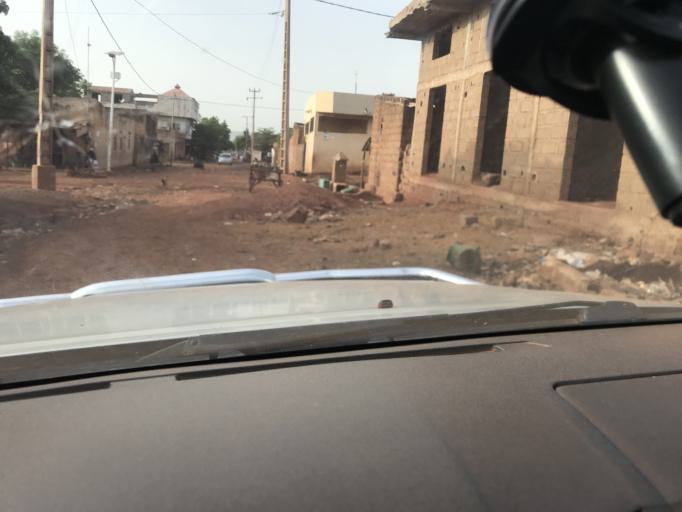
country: ML
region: Bamako
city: Bamako
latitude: 12.5928
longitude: -8.0079
